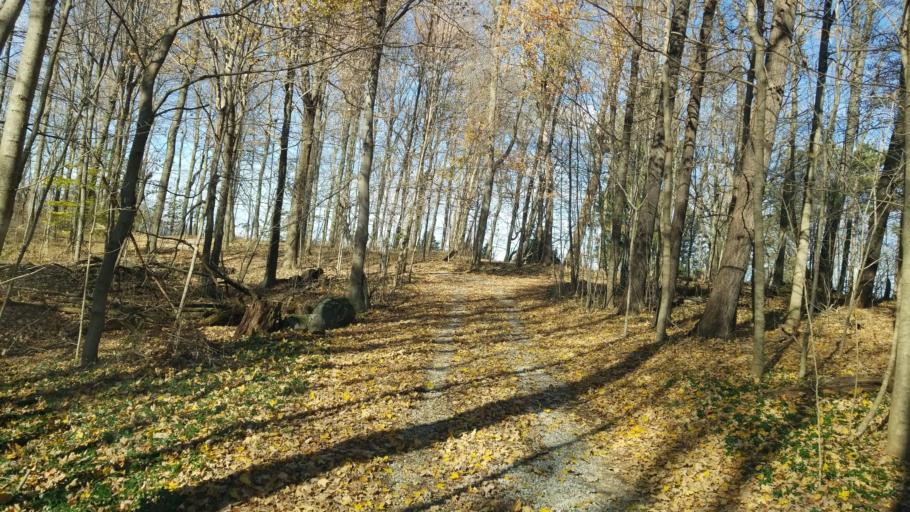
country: US
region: Ohio
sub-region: Sandusky County
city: Bellville
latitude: 40.6519
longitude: -82.4505
